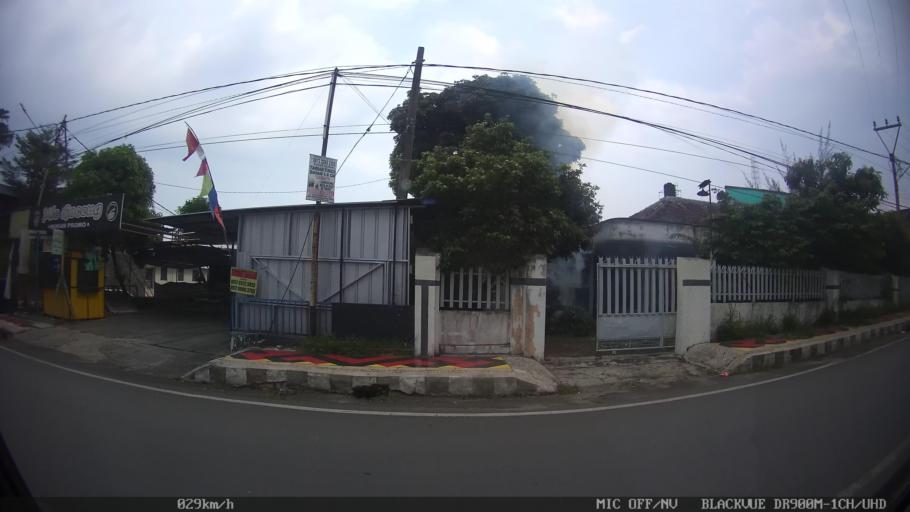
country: ID
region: Lampung
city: Bandarlampung
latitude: -5.4269
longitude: 105.2698
